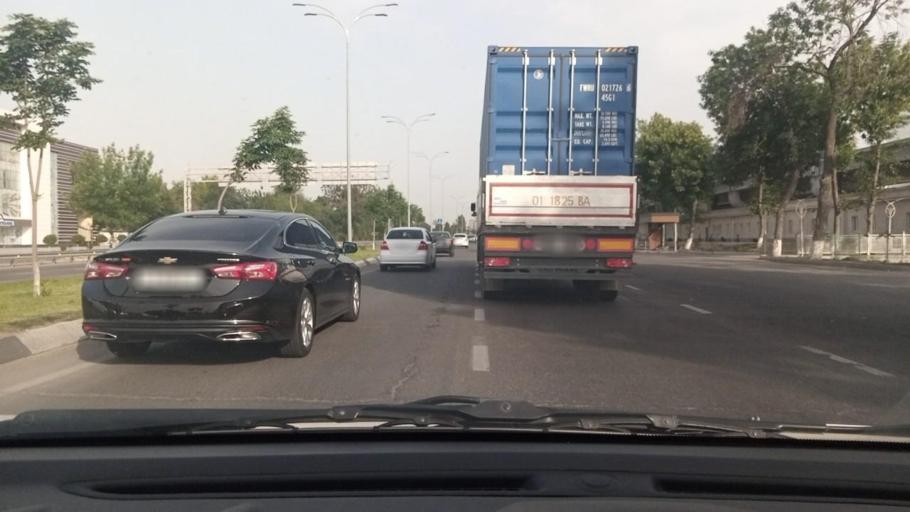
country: UZ
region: Toshkent
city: Salor
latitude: 41.2989
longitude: 69.3486
